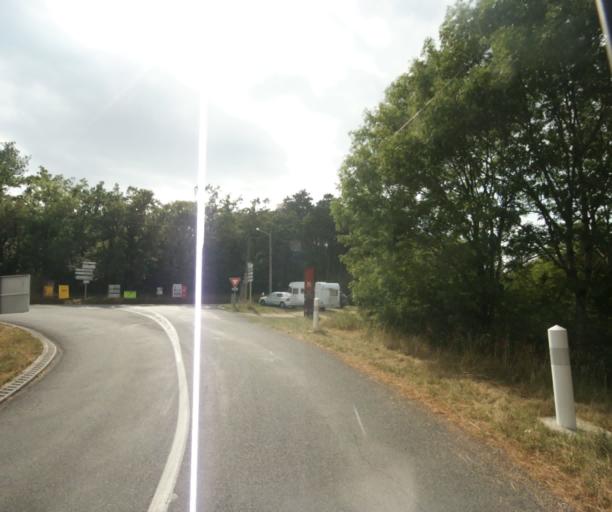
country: FR
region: Midi-Pyrenees
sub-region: Departement du Tarn
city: Soreze
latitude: 43.4394
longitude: 2.0353
